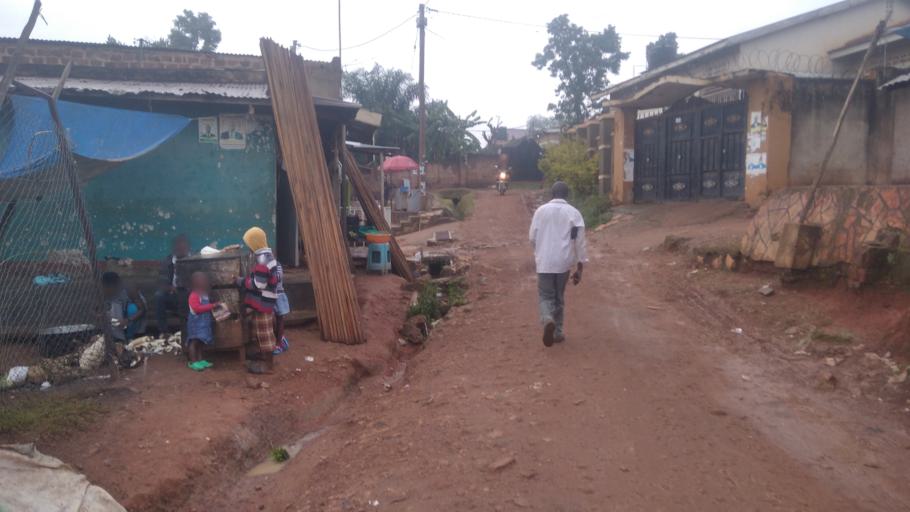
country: UG
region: Central Region
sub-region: Wakiso District
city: Bweyogerere
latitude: 0.3574
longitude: 32.6560
